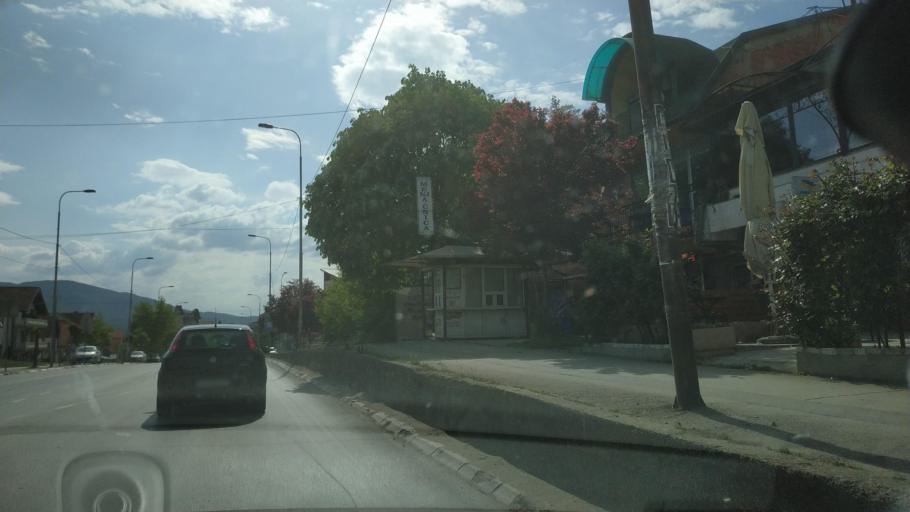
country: RS
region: Central Serbia
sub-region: Toplicki Okrug
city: Prokuplje
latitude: 43.2397
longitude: 21.6027
